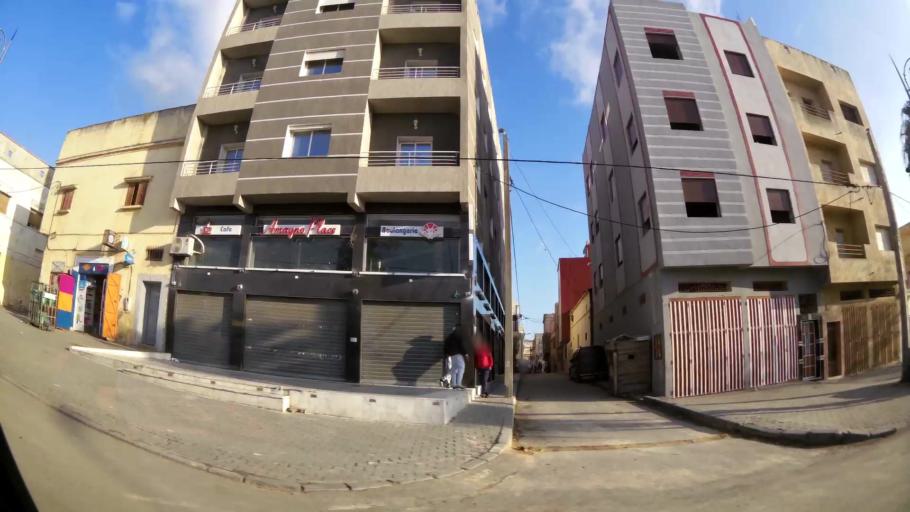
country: MA
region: Chaouia-Ouardigha
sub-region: Settat Province
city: Settat
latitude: 33.0041
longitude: -7.6111
